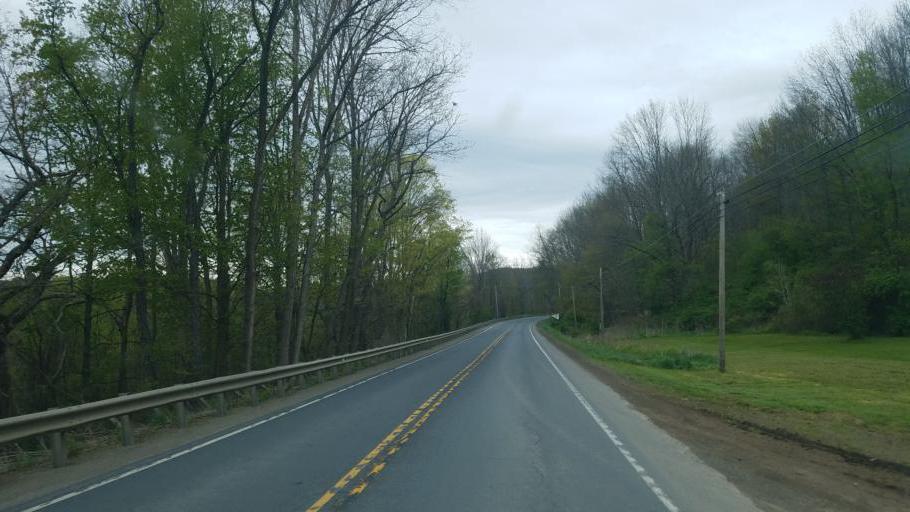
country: US
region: Pennsylvania
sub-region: Tioga County
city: Westfield
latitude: 41.9498
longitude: -77.4692
